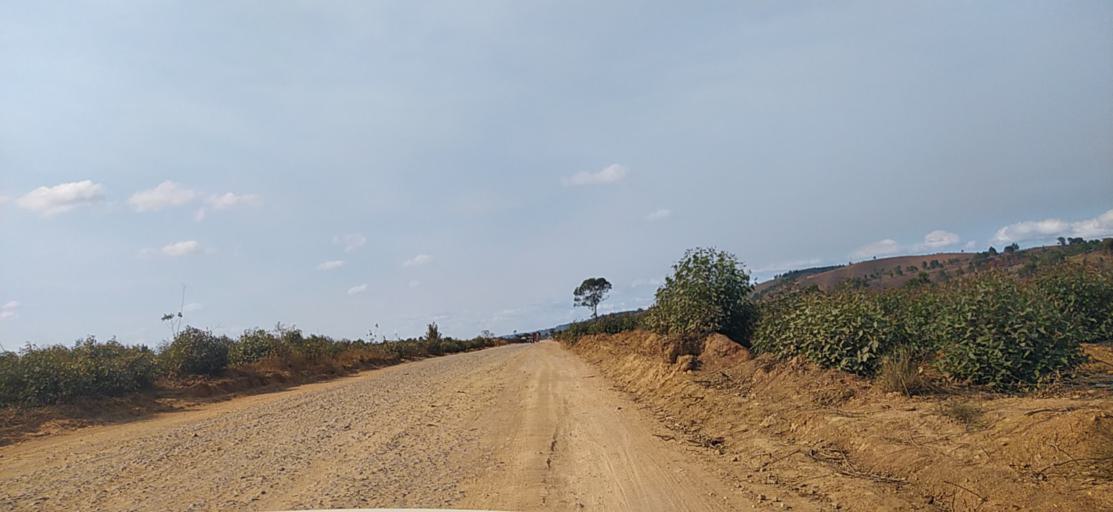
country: MG
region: Alaotra Mangoro
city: Moramanga
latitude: -18.6791
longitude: 48.2725
